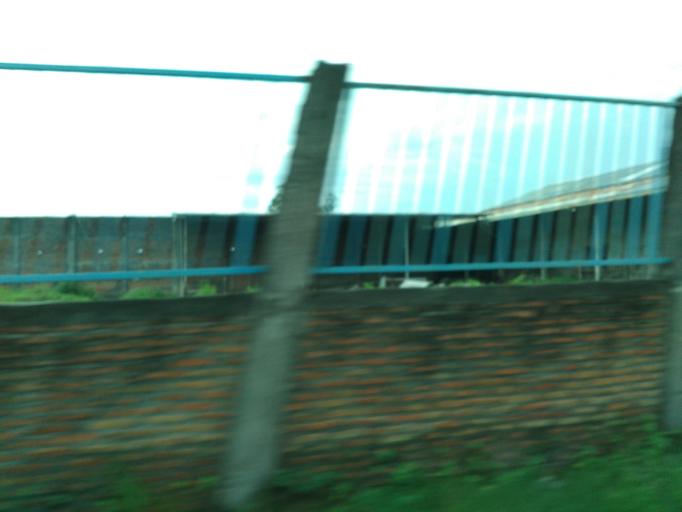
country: ID
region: Central Java
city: Gatak
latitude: -7.5782
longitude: 110.7157
